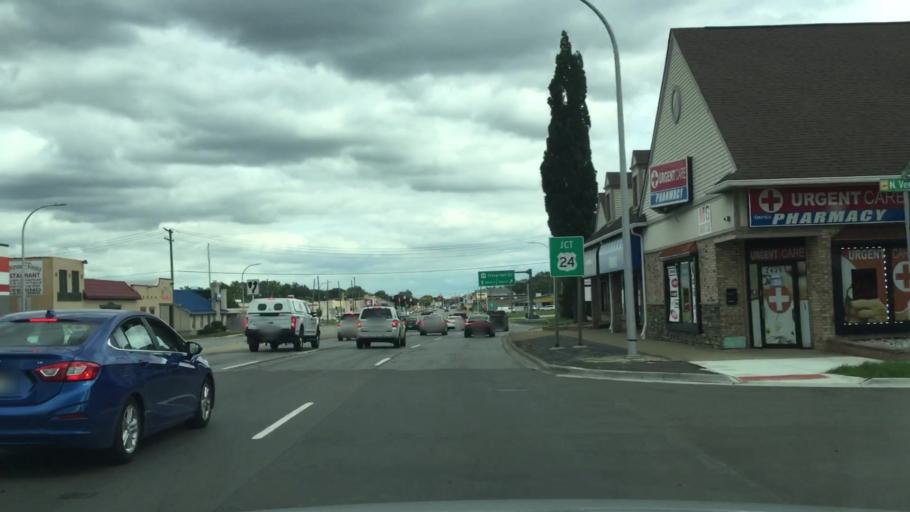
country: US
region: Michigan
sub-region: Wayne County
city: Dearborn Heights
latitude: 42.3269
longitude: -83.2761
